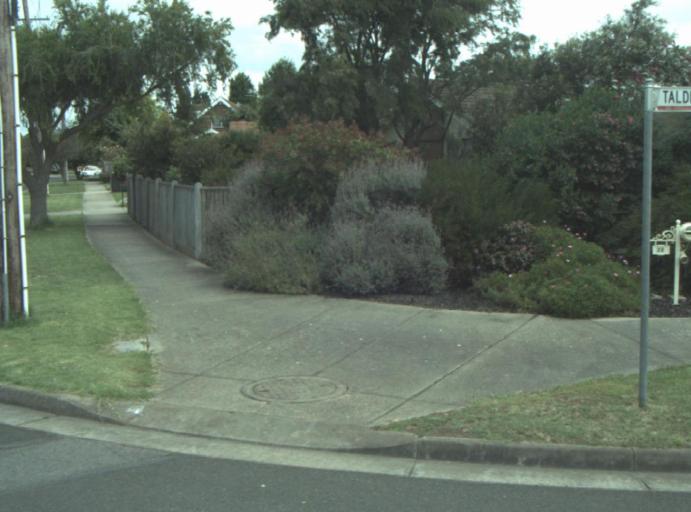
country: AU
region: Victoria
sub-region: Greater Geelong
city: Breakwater
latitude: -38.1894
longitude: 144.3403
